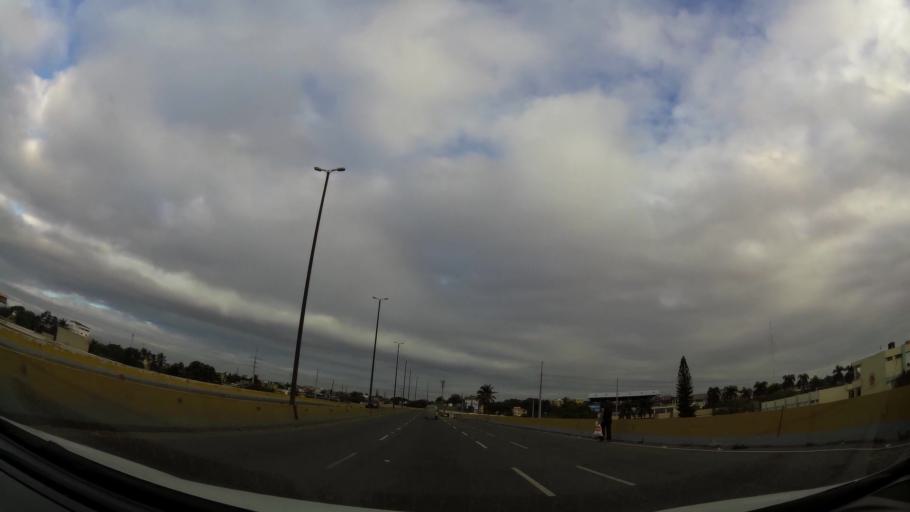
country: DO
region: San Cristobal
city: El Carril
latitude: 18.4262
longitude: -69.9893
